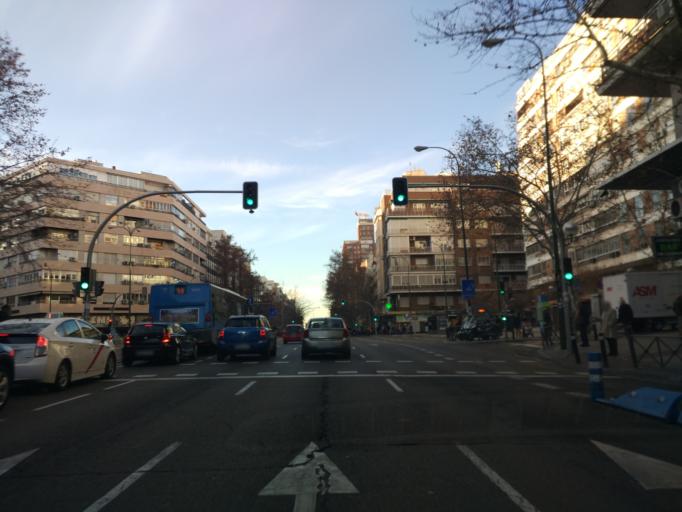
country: ES
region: Madrid
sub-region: Provincia de Madrid
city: Salamanca
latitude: 40.4343
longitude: -3.6740
